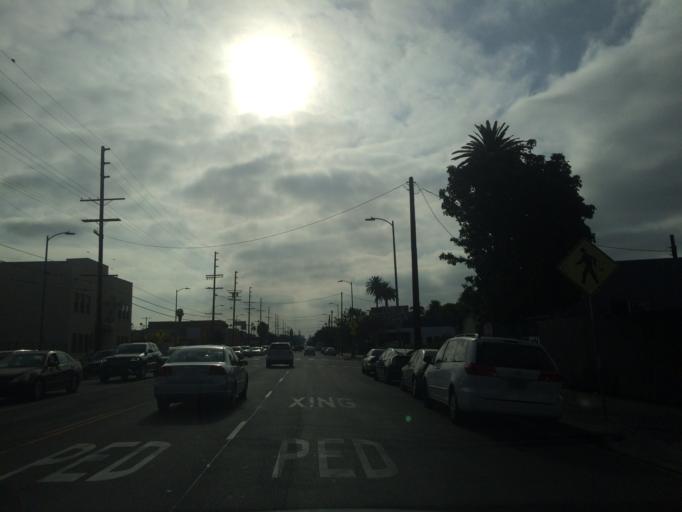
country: US
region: California
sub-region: Los Angeles County
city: View Park-Windsor Hills
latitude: 34.0324
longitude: -118.3492
